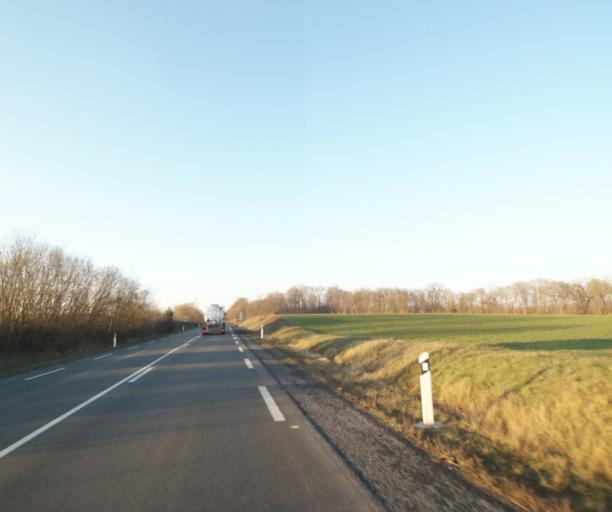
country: FR
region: Champagne-Ardenne
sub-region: Departement de la Haute-Marne
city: Bienville
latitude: 48.5483
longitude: 5.0663
